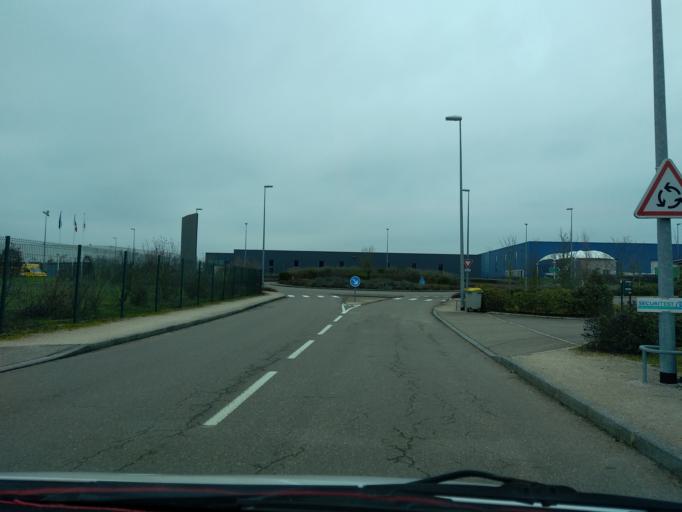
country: FR
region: Bourgogne
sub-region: Departement de la Cote-d'Or
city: Saint-Apollinaire
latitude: 47.3416
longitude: 5.0654
